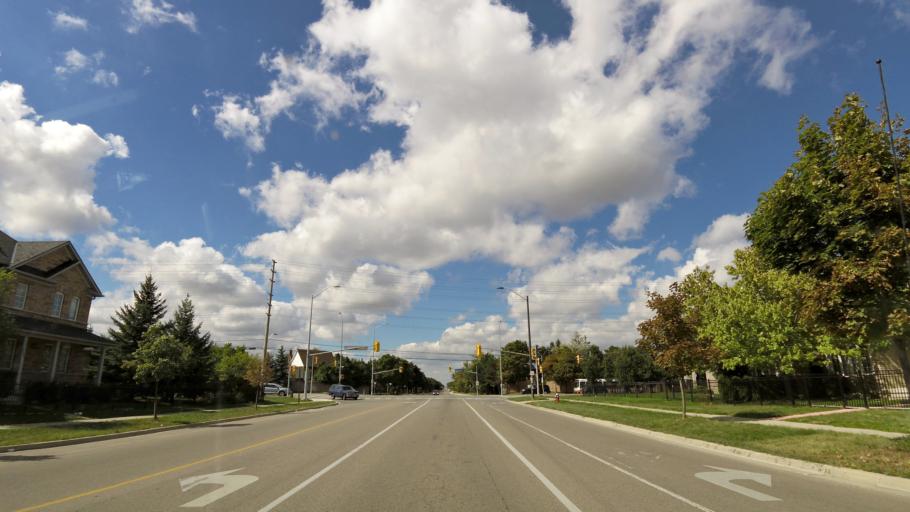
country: CA
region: Ontario
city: Mississauga
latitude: 43.5638
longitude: -79.7486
